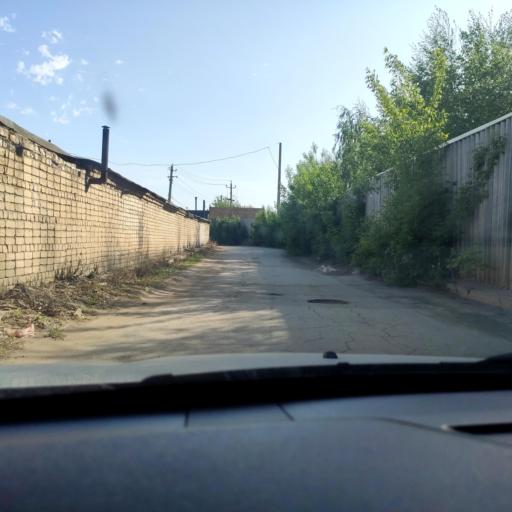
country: RU
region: Samara
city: Smyshlyayevka
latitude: 53.2185
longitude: 50.2791
